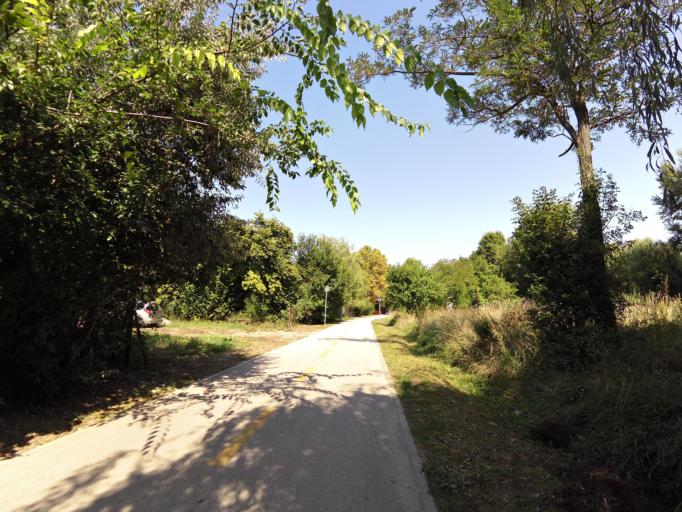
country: HU
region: Veszprem
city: Tihany
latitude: 46.8969
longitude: 17.8928
